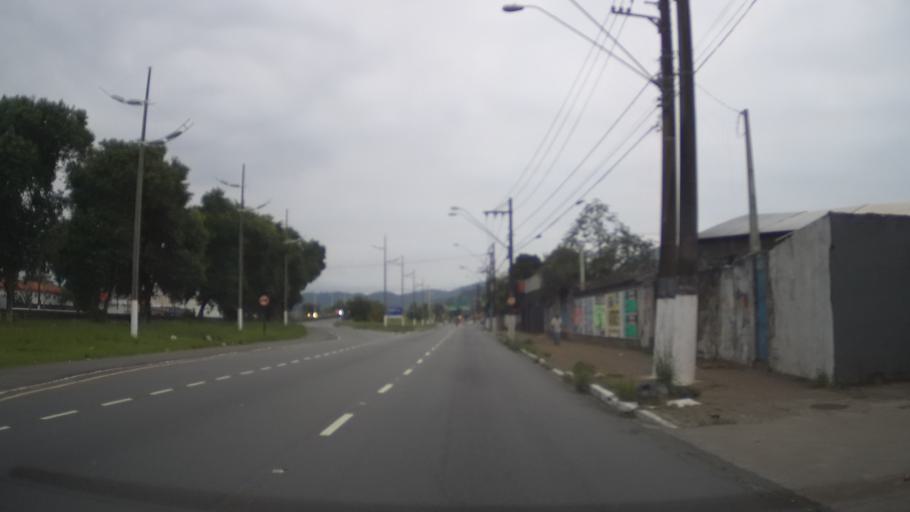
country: BR
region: Sao Paulo
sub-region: Praia Grande
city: Praia Grande
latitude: -24.0051
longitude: -46.4273
